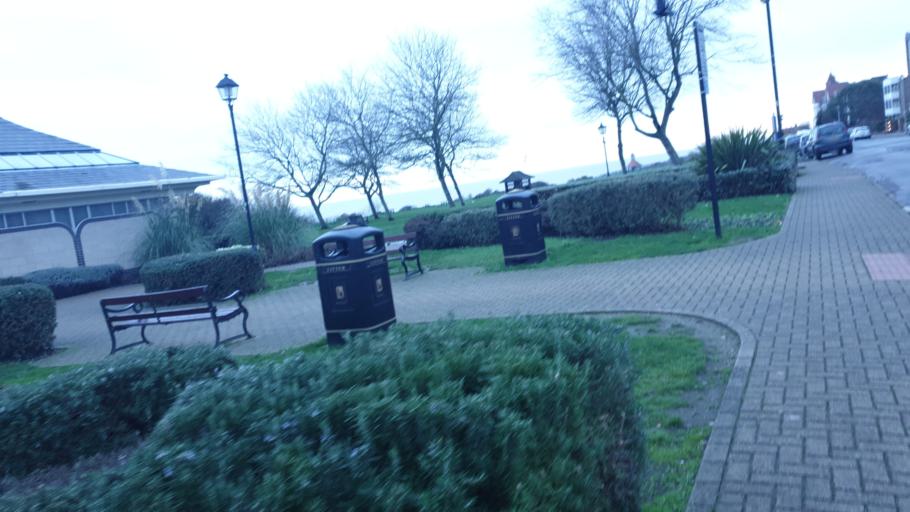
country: GB
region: England
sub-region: Essex
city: Frinton-on-Sea
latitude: 51.8291
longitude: 1.2466
